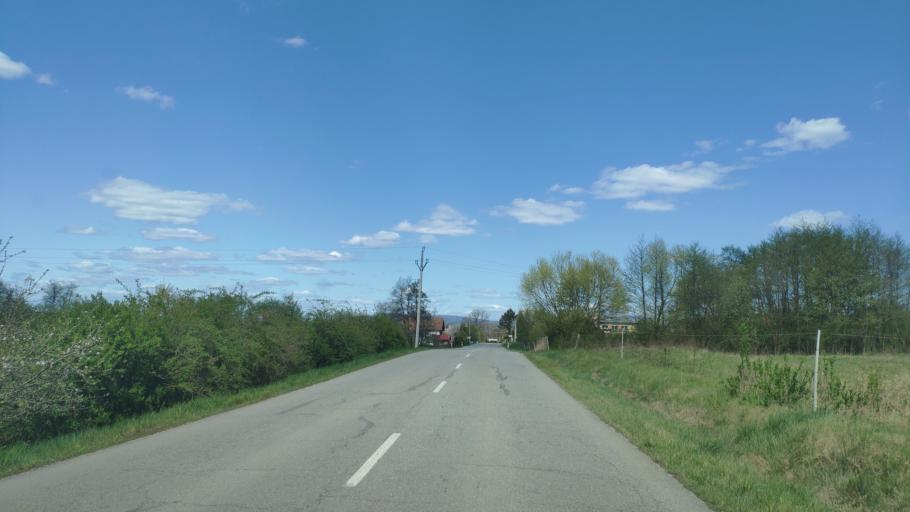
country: SK
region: Kosicky
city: Kosice
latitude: 48.6627
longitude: 21.4086
